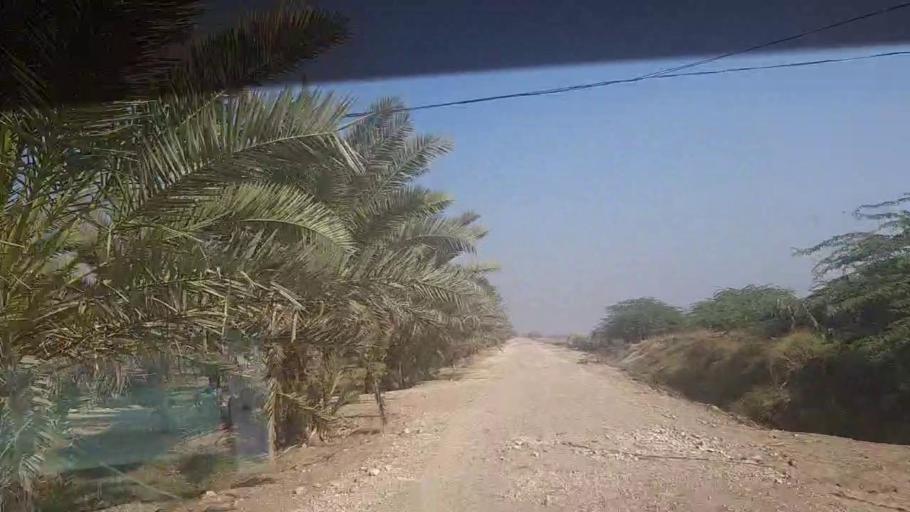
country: PK
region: Sindh
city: Khairpur
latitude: 27.4610
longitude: 68.7293
